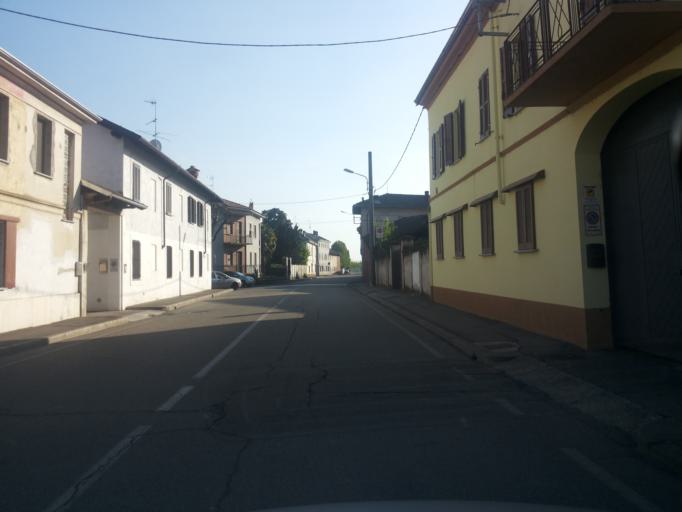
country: IT
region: Lombardy
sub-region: Provincia di Pavia
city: Cilavegna
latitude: 45.3077
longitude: 8.7400
